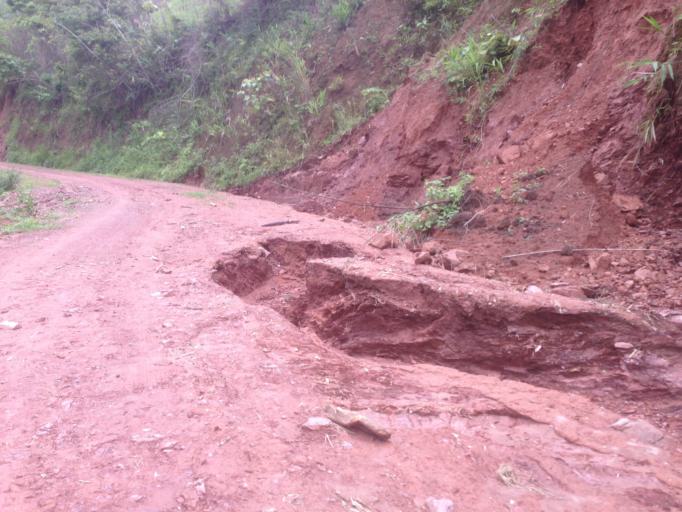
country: TH
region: Nan
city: Bo Kluea
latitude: 19.3911
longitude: 101.3283
